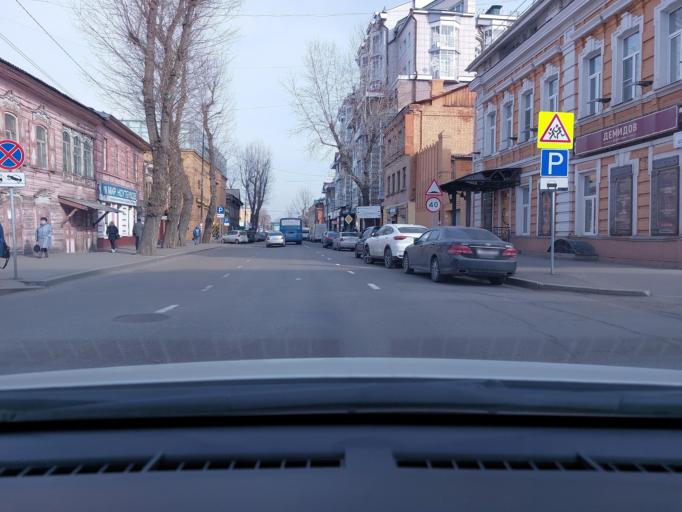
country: RU
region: Irkutsk
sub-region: Irkutskiy Rayon
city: Irkutsk
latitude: 52.2801
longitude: 104.2897
